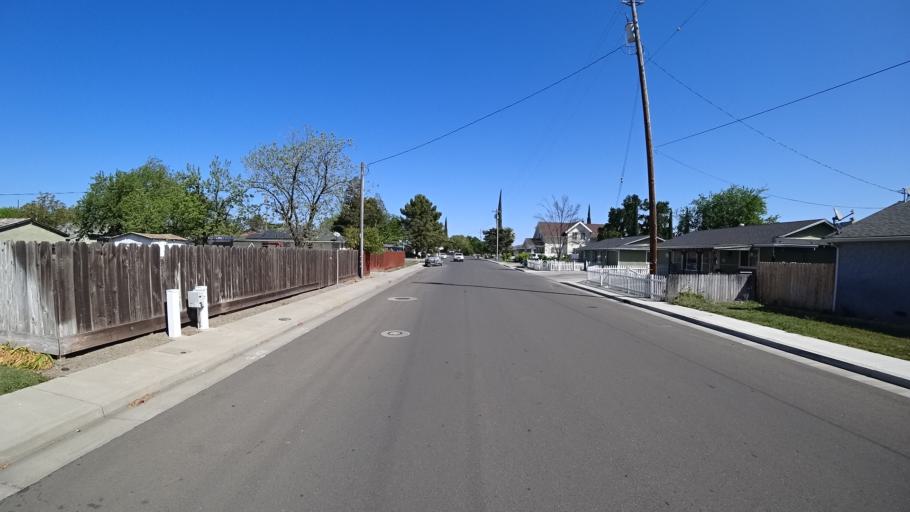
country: US
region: California
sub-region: Glenn County
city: Orland
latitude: 39.7493
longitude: -122.1781
